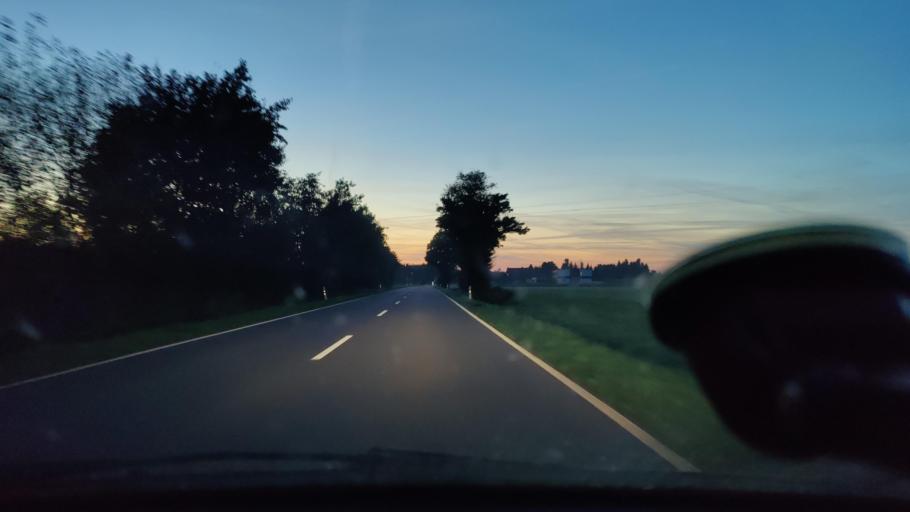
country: DE
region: North Rhine-Westphalia
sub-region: Regierungsbezirk Munster
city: Sudlohn
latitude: 51.9021
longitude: 6.8682
